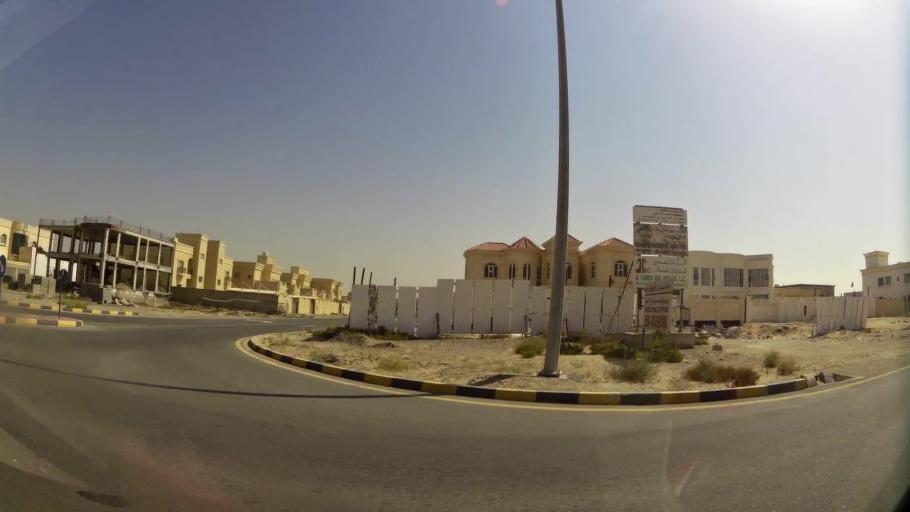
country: AE
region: Ajman
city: Ajman
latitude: 25.4120
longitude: 55.5303
